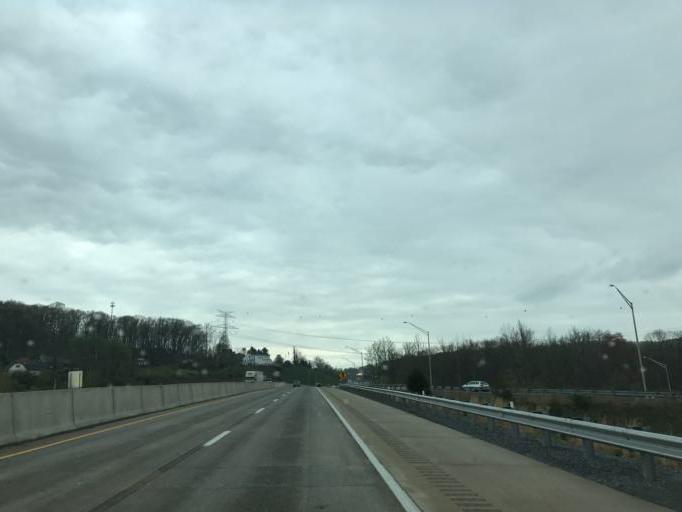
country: US
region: Pennsylvania
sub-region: Lancaster County
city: Adamstown
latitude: 40.2478
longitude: -76.0370
